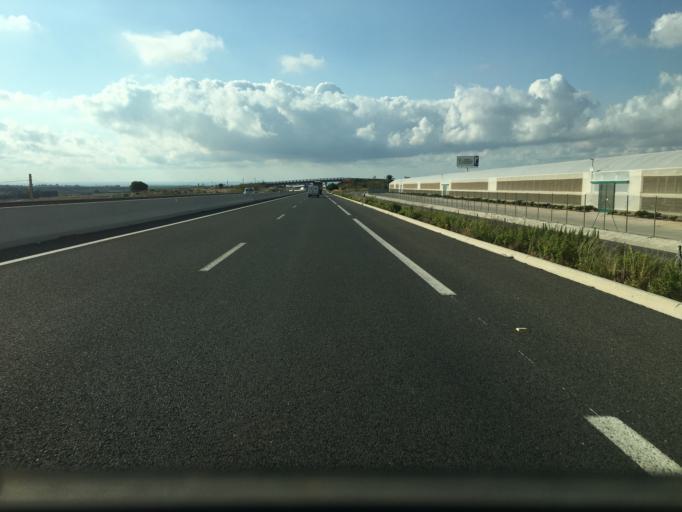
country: ES
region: Murcia
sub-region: Murcia
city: San Javier
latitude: 37.8699
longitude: -0.9088
